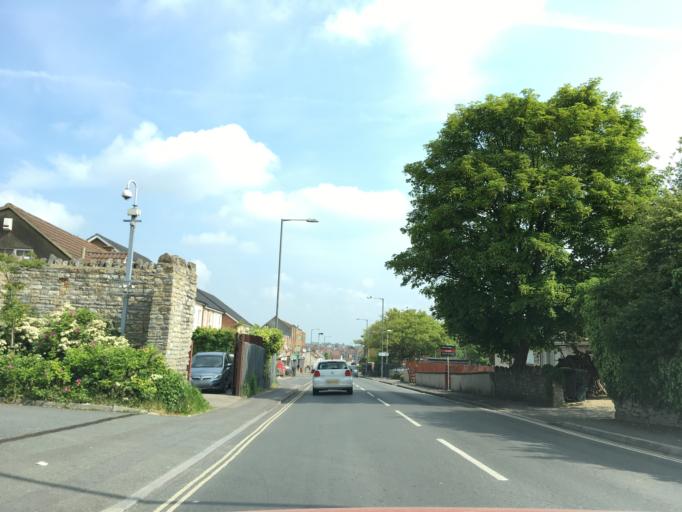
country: GB
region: England
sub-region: North Somerset
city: Dundry
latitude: 51.4079
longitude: -2.6216
